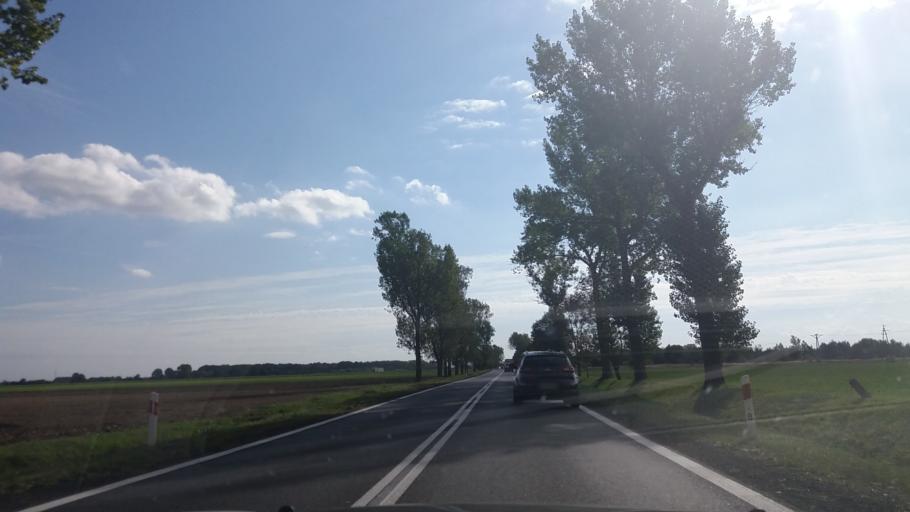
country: PL
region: Lower Silesian Voivodeship
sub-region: Powiat legnicki
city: Prochowice
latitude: 51.3251
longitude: 16.3137
